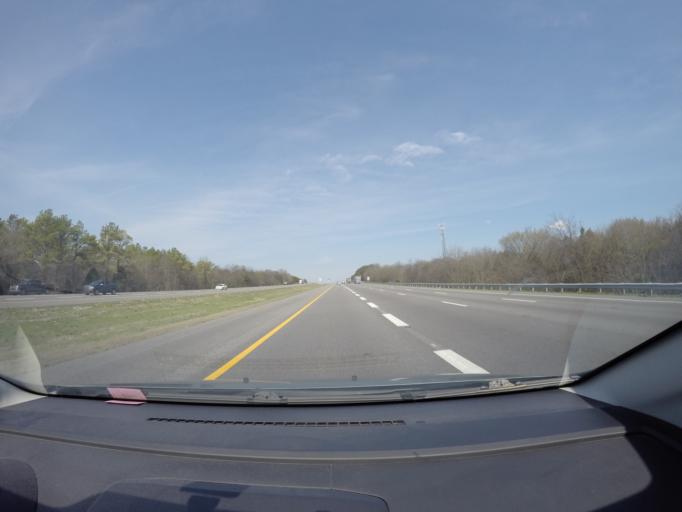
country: US
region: Tennessee
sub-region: Rutherford County
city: Smyrna
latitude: 35.9168
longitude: -86.5117
